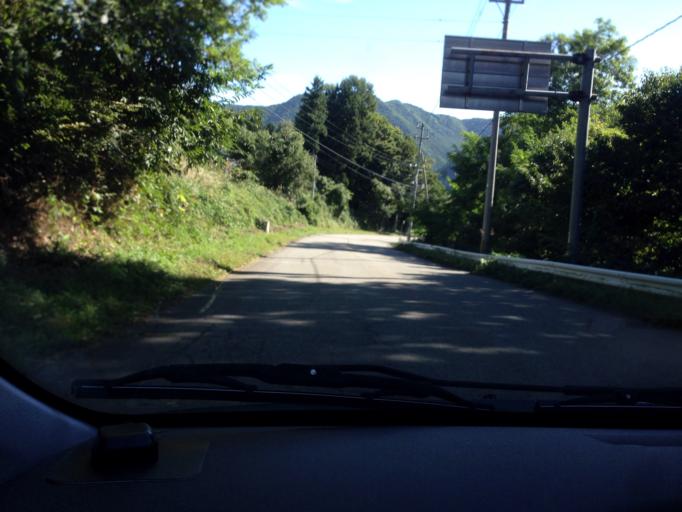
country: JP
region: Fukushima
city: Inawashiro
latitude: 37.5784
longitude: 140.1205
